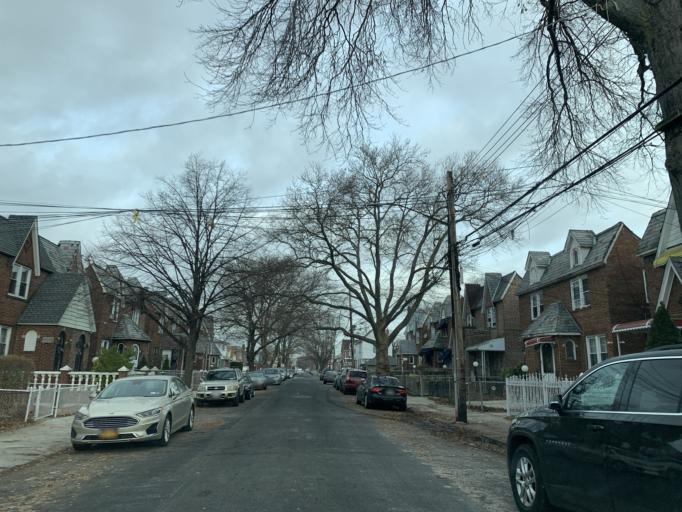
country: US
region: New York
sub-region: Queens County
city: Jamaica
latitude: 40.6808
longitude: -73.8093
